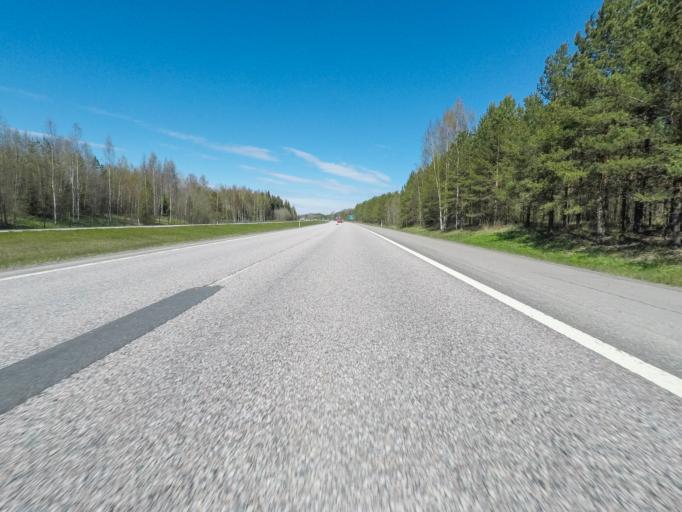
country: FI
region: Uusimaa
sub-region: Helsinki
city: Hyvinge
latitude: 60.6447
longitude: 24.8075
